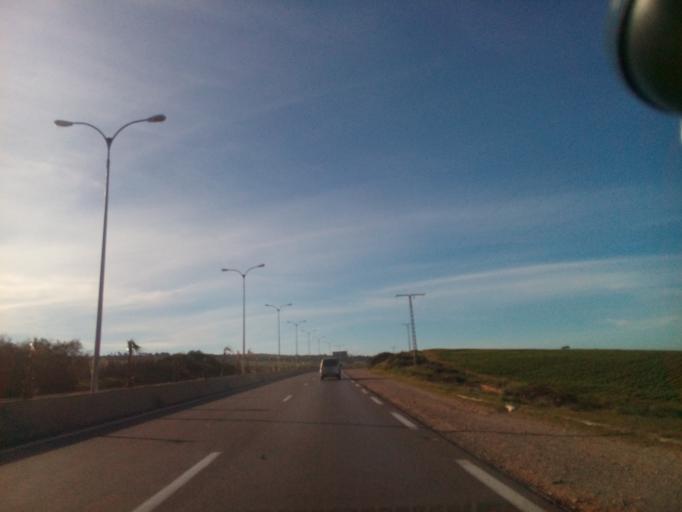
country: DZ
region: Mostaganem
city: Mostaganem
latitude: 35.8278
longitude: -0.0117
